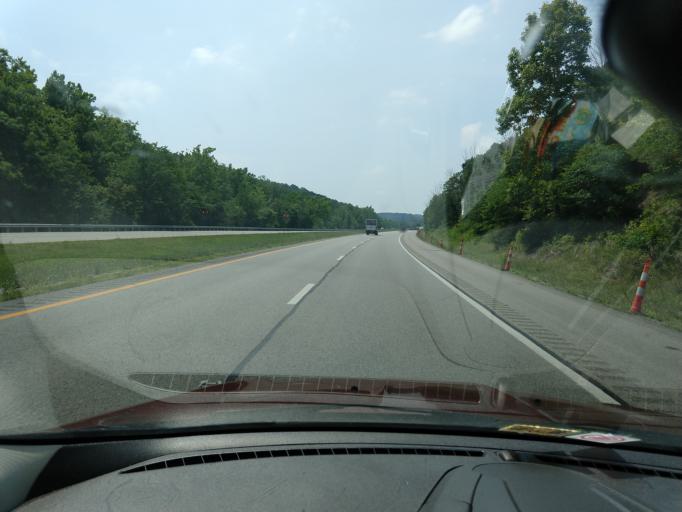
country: US
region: West Virginia
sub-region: Jackson County
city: Ripley
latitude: 38.7036
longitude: -81.6414
